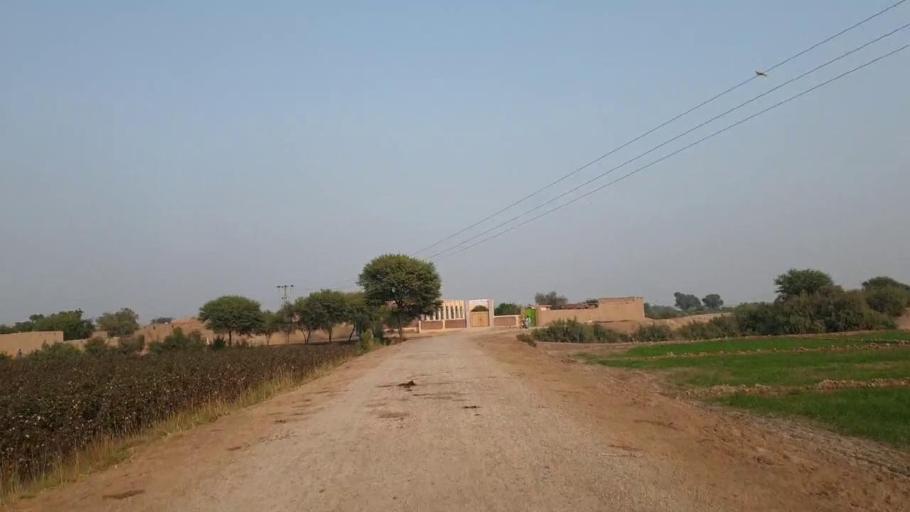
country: PK
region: Sindh
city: Bhan
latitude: 26.5036
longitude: 67.7576
